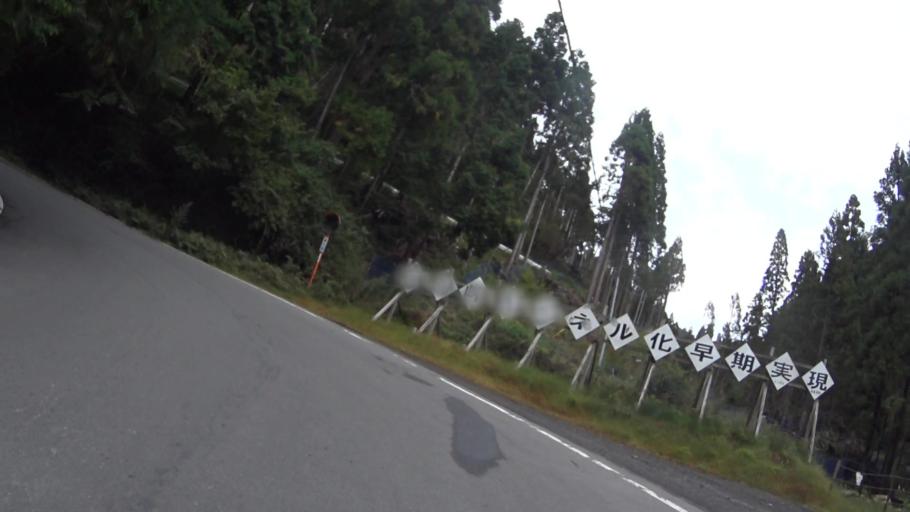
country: JP
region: Kyoto
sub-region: Kyoto-shi
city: Kamigyo-ku
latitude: 35.1469
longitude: 135.7832
